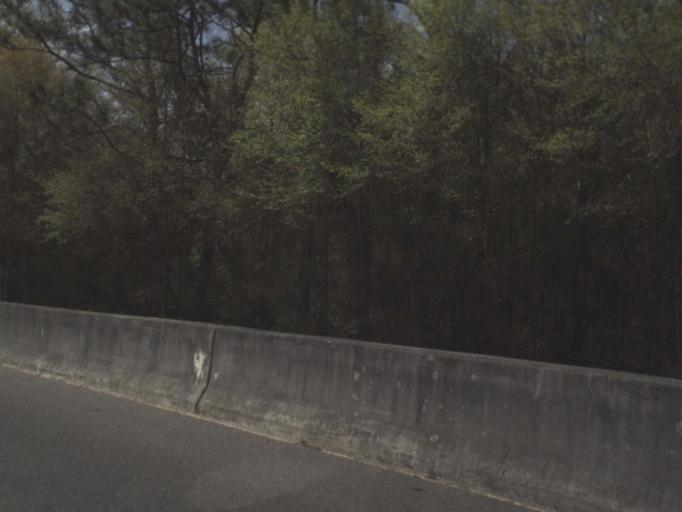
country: US
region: Florida
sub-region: Okaloosa County
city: Crestview
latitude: 30.7358
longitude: -86.6540
